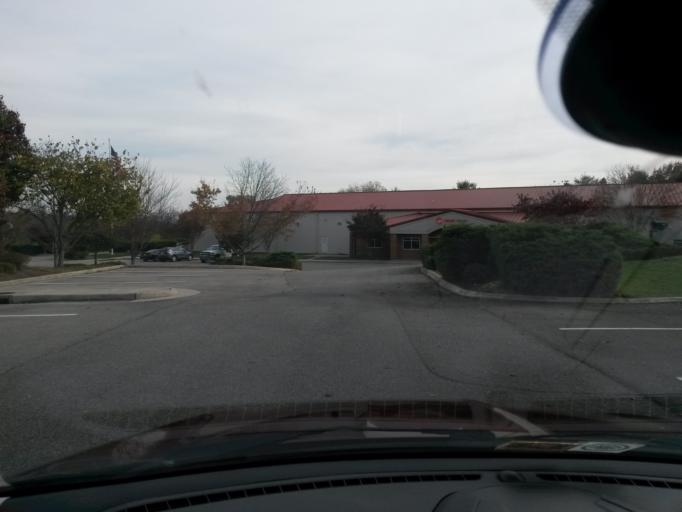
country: US
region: Virginia
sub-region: Roanoke County
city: Hollins
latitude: 37.3160
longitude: -79.9839
